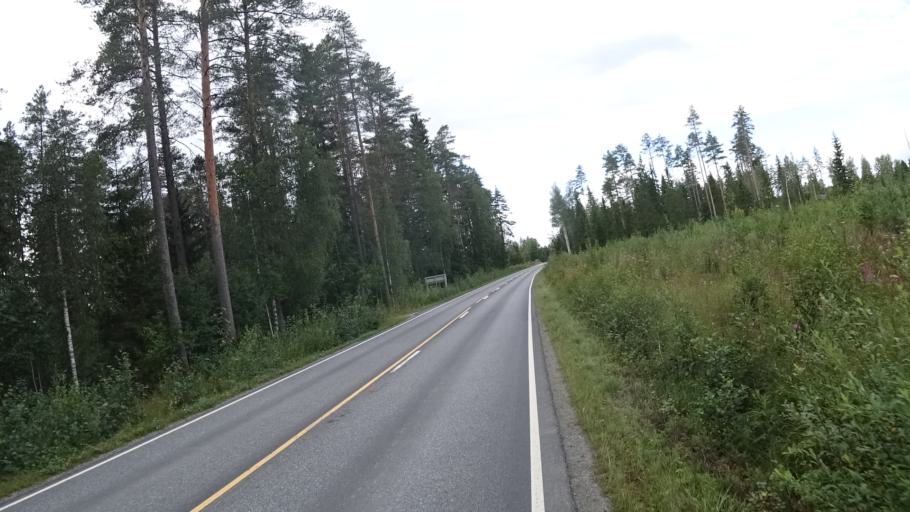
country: FI
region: North Karelia
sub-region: Joensuu
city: Ilomantsi
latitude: 62.6504
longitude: 30.9743
